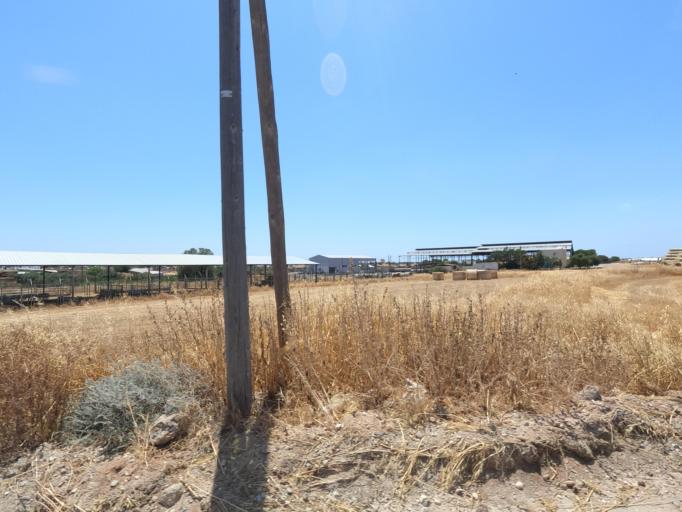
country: CY
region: Larnaka
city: Xylotymbou
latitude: 35.0190
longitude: 33.7293
